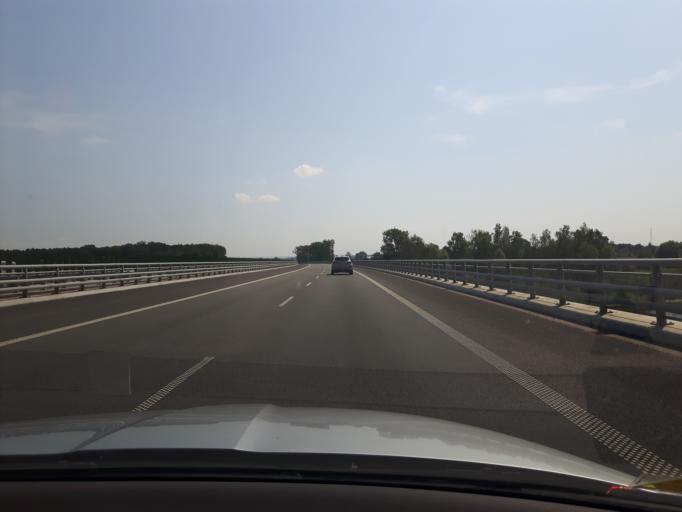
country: PL
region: Warmian-Masurian Voivodeship
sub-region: Powiat elblaski
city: Gronowo Elblaskie
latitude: 54.1658
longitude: 19.2400
